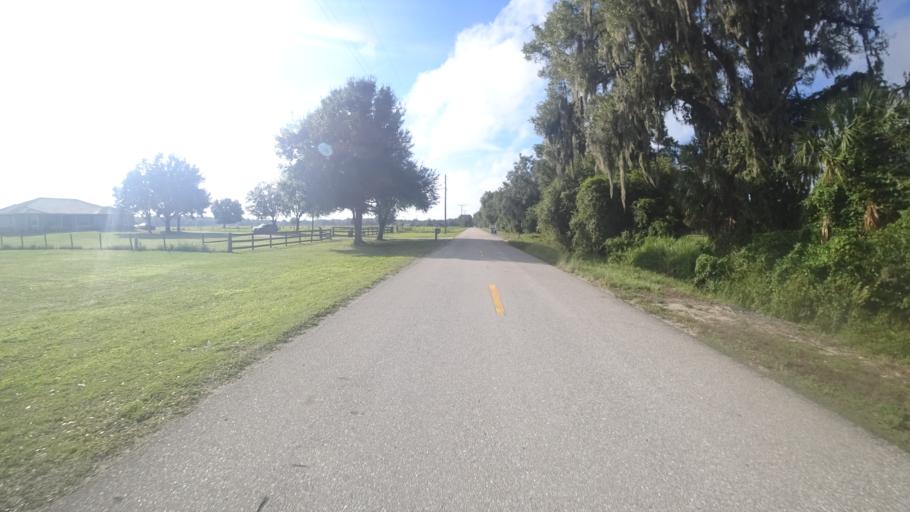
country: US
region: Florida
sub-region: Manatee County
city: Ellenton
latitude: 27.5694
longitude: -82.4089
